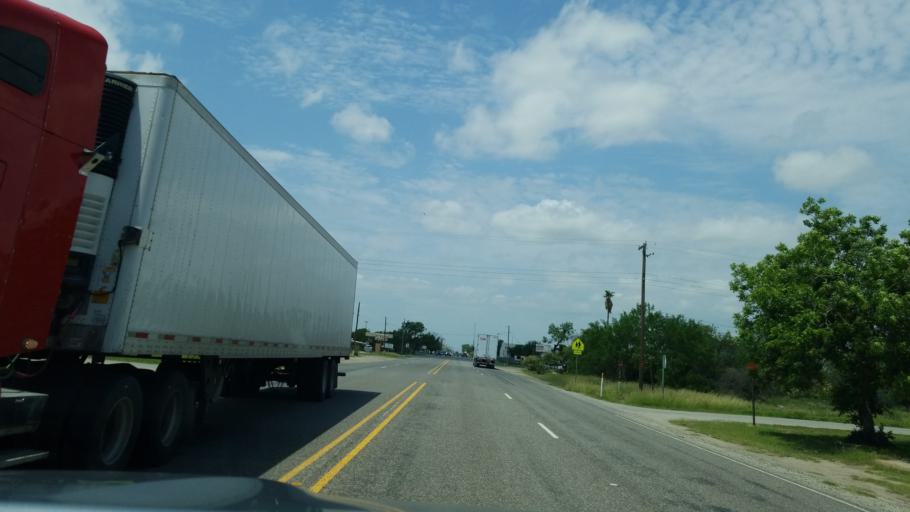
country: US
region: Texas
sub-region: Zavala County
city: La Pryor
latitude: 28.9453
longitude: -99.8380
